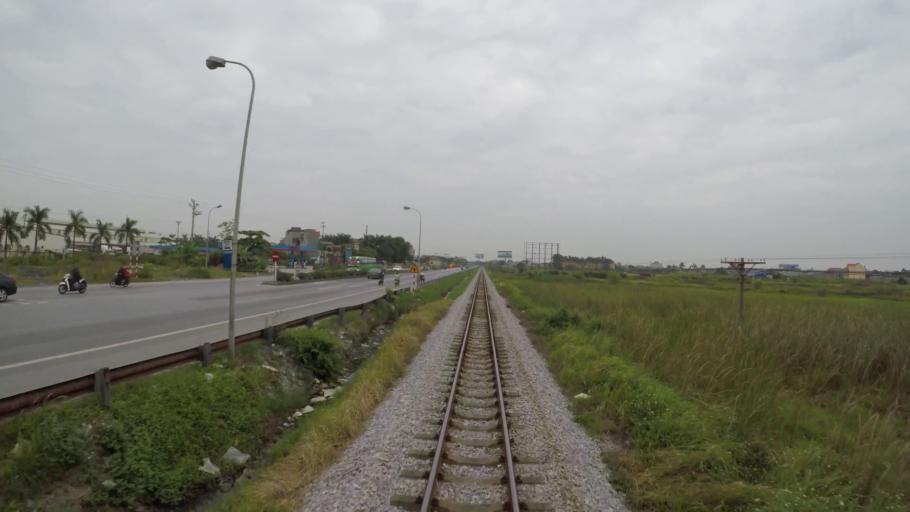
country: VN
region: Hai Duong
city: Phu Thai
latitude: 20.9250
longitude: 106.5575
